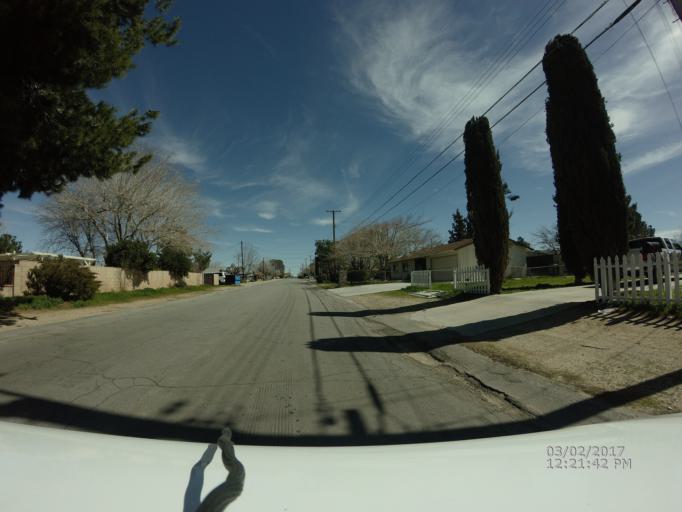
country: US
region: California
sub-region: Los Angeles County
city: Quartz Hill
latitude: 34.6493
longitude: -118.2227
